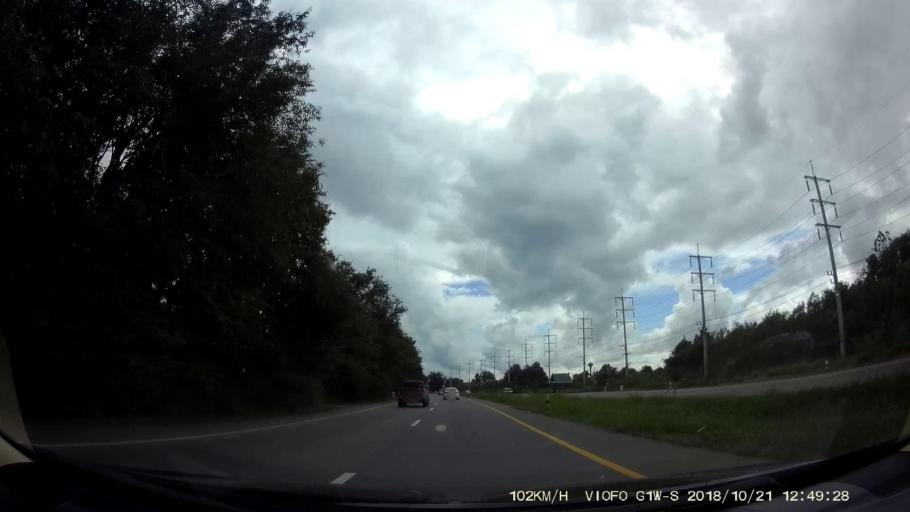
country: TH
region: Nakhon Ratchasima
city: Amphoe Sikhiu
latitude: 14.8958
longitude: 101.6845
